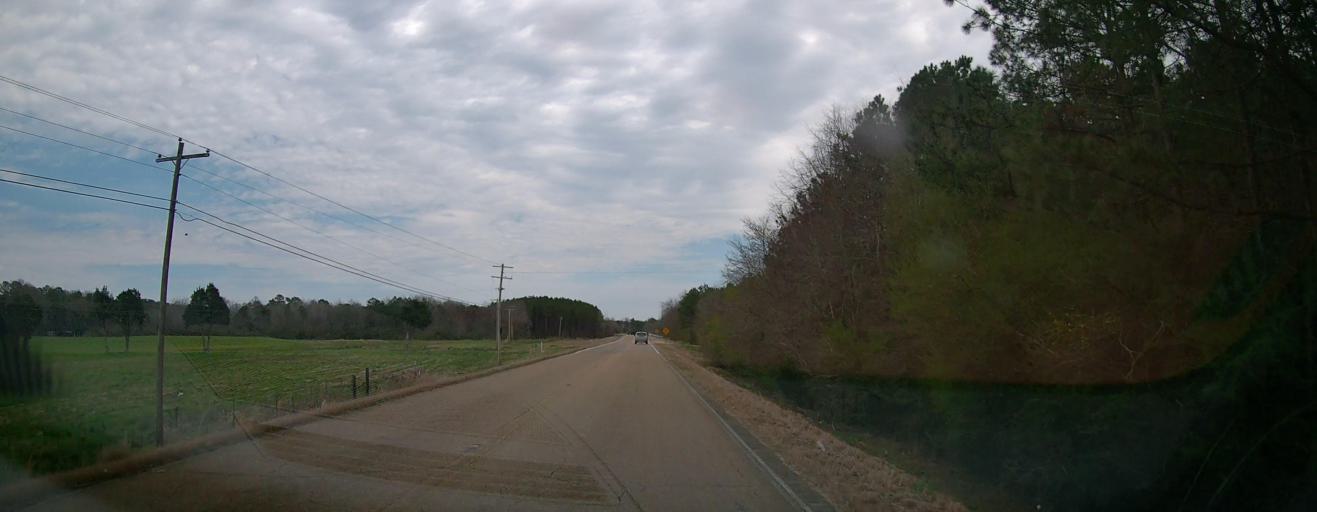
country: US
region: Mississippi
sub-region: Itawamba County
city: Fulton
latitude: 34.2329
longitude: -88.2522
